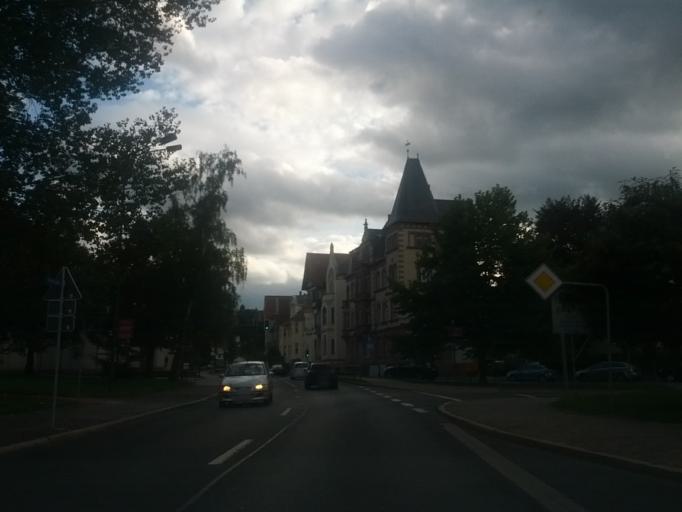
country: DE
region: Thuringia
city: Eisenach
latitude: 50.9700
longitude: 10.3244
